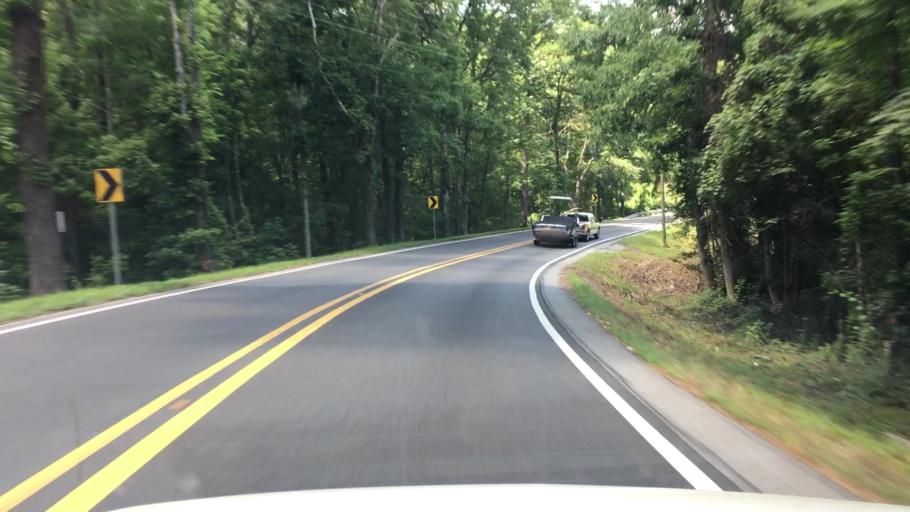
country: US
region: Arkansas
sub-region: Clark County
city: Arkadelphia
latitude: 34.2573
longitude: -93.1301
